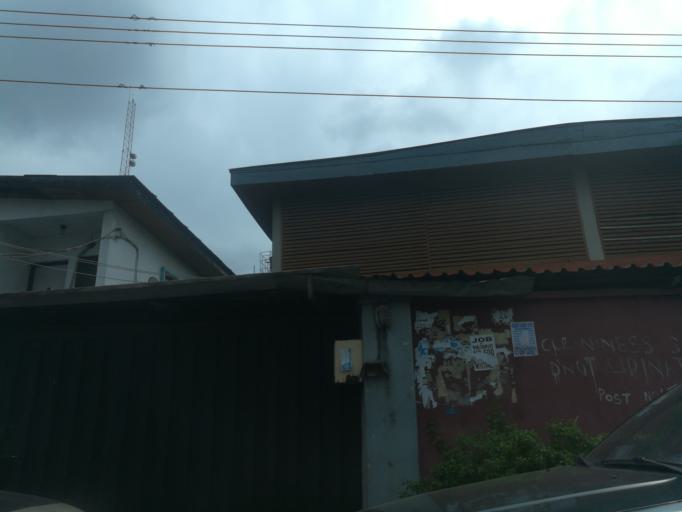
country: NG
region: Lagos
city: Ikeja
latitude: 6.5987
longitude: 3.3393
